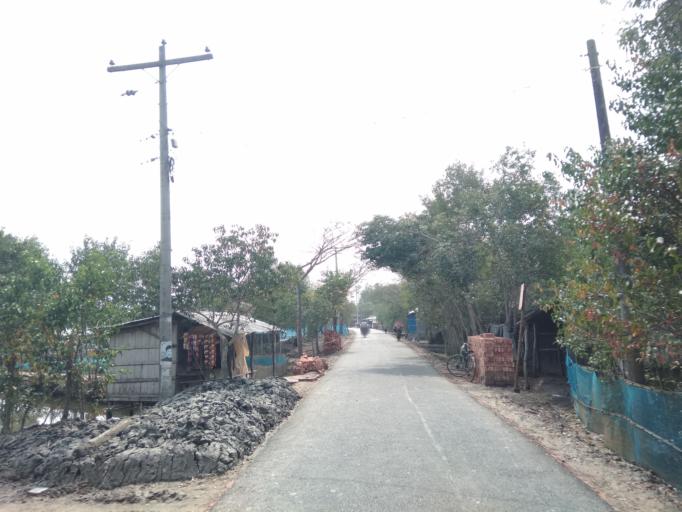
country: IN
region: West Bengal
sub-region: North 24 Parganas
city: Gosaba
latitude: 22.2659
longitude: 89.2182
